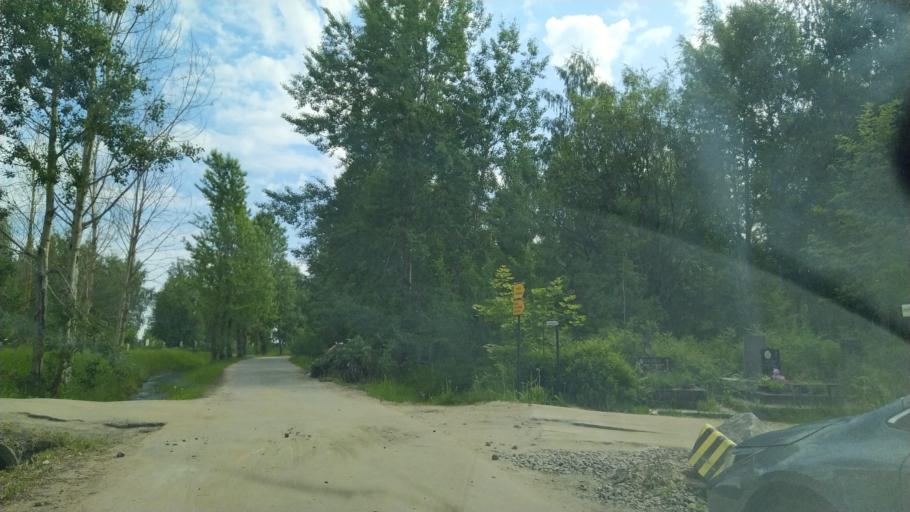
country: RU
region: St.-Petersburg
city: Dachnoye
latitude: 59.7728
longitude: 30.2701
